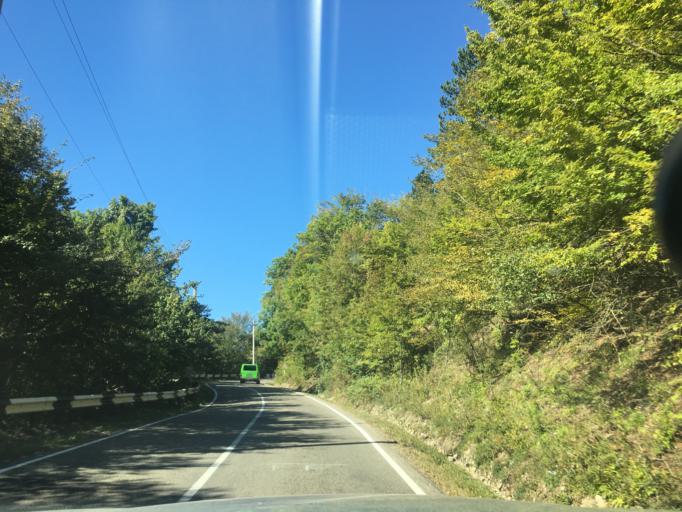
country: GE
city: Didi Lilo
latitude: 41.8721
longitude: 44.9116
